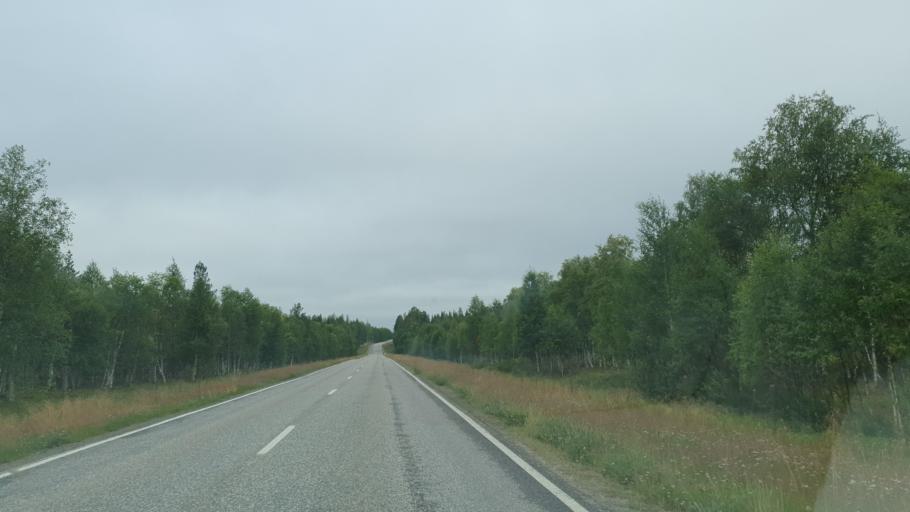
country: FI
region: Lapland
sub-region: Pohjois-Lappi
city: Sodankylae
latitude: 67.3964
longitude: 26.7249
